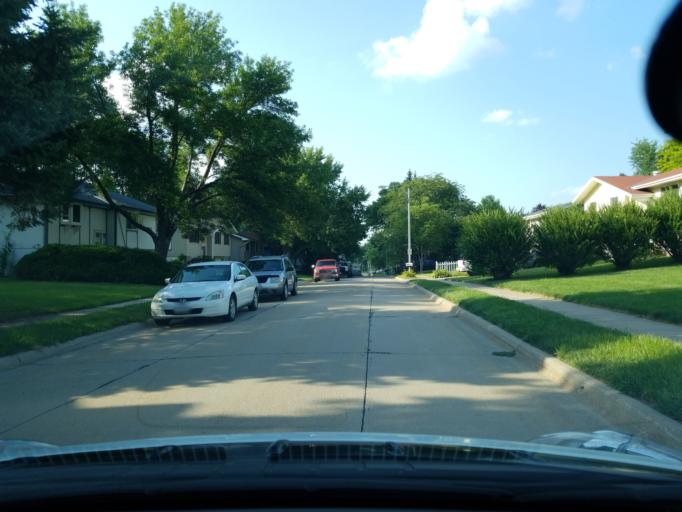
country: US
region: Nebraska
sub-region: Sarpy County
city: Offutt Air Force Base
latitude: 41.1296
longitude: -95.9628
